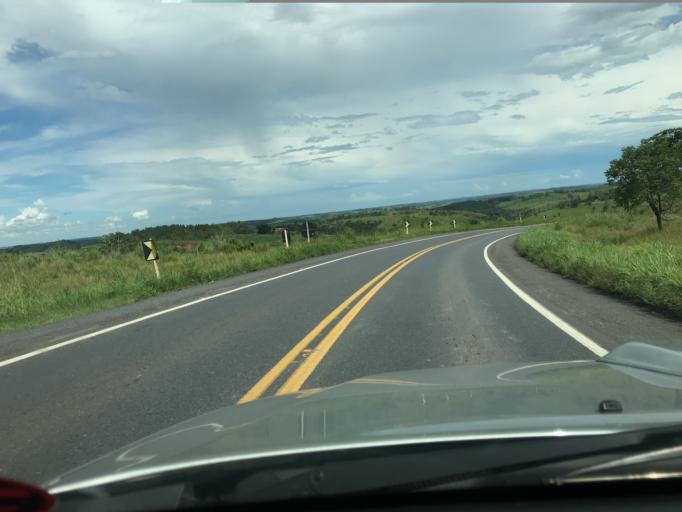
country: BR
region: Minas Gerais
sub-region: Campos Altos
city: Campos Altos
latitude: -19.7962
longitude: -46.0341
